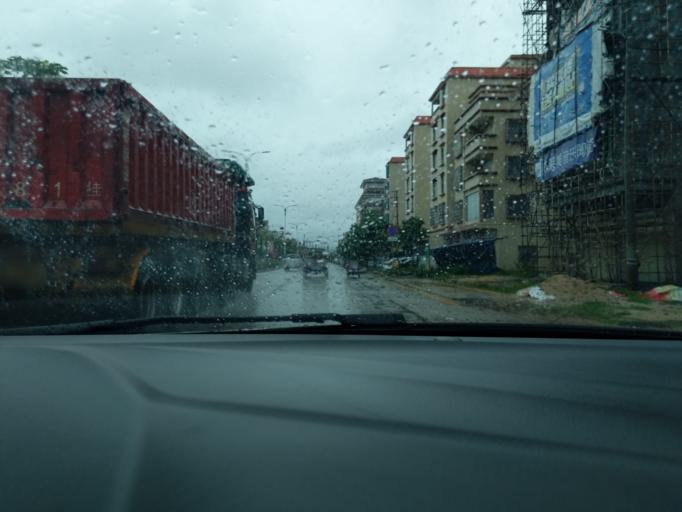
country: CN
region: Guangdong
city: Pingshi
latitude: 22.2049
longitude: 112.3261
